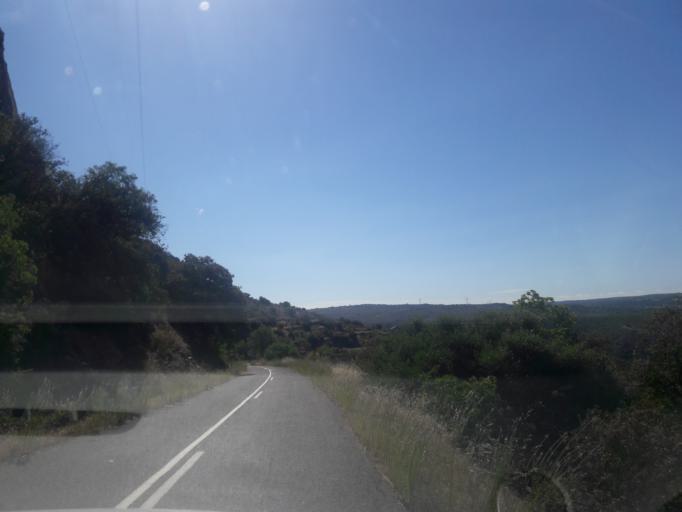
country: ES
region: Castille and Leon
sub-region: Provincia de Salamanca
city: Saucelle
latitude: 41.0325
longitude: -6.7611
